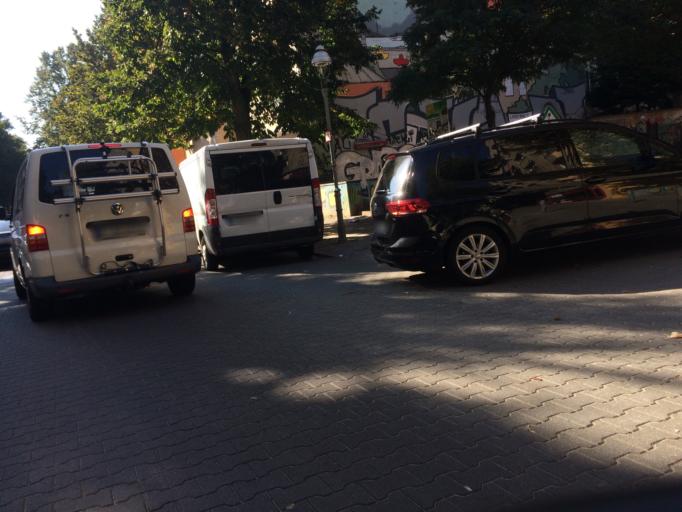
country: DE
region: Berlin
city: Berlin Treptow
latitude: 52.4918
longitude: 13.4258
